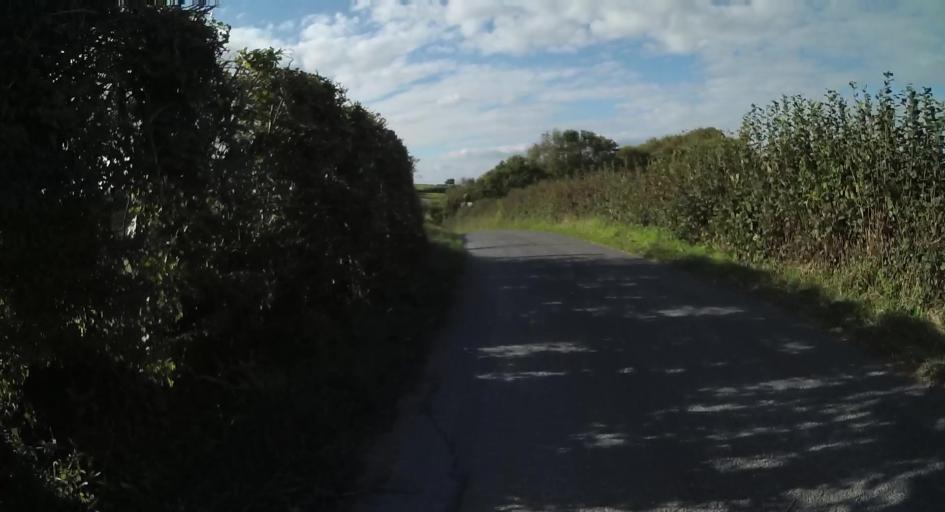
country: GB
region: England
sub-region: Isle of Wight
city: Newport
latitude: 50.6484
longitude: -1.2997
